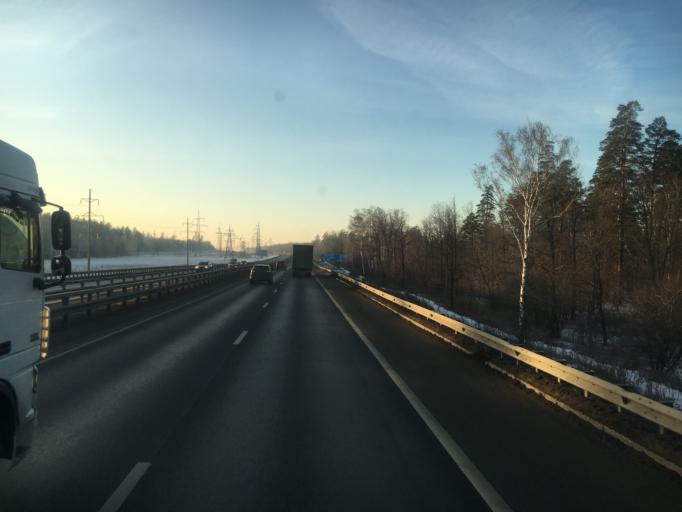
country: RU
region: Samara
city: Pribrezhnyy
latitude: 53.5180
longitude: 49.8305
